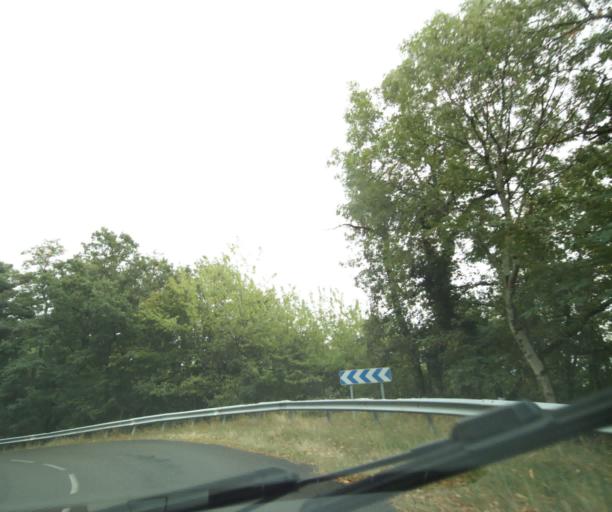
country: FR
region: Auvergne
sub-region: Departement du Puy-de-Dome
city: Durtol
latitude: 45.7938
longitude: 3.0404
